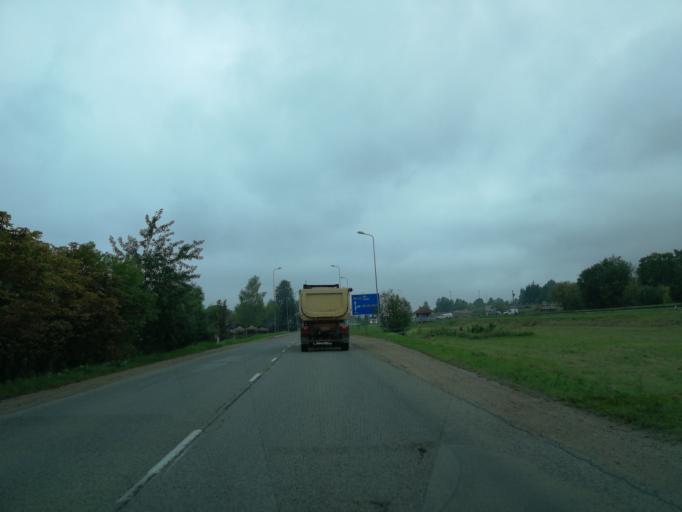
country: LV
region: Jekabpils Rajons
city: Jekabpils
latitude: 56.5031
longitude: 25.8926
